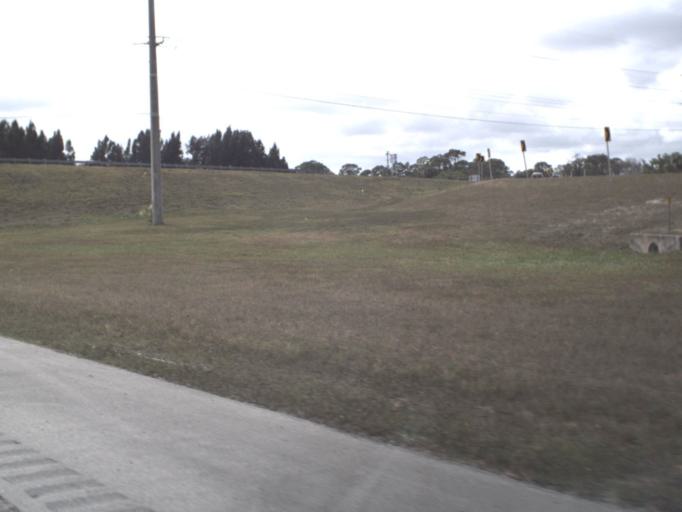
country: US
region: Florida
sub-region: Brevard County
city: South Patrick Shores
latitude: 28.2050
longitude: -80.6607
